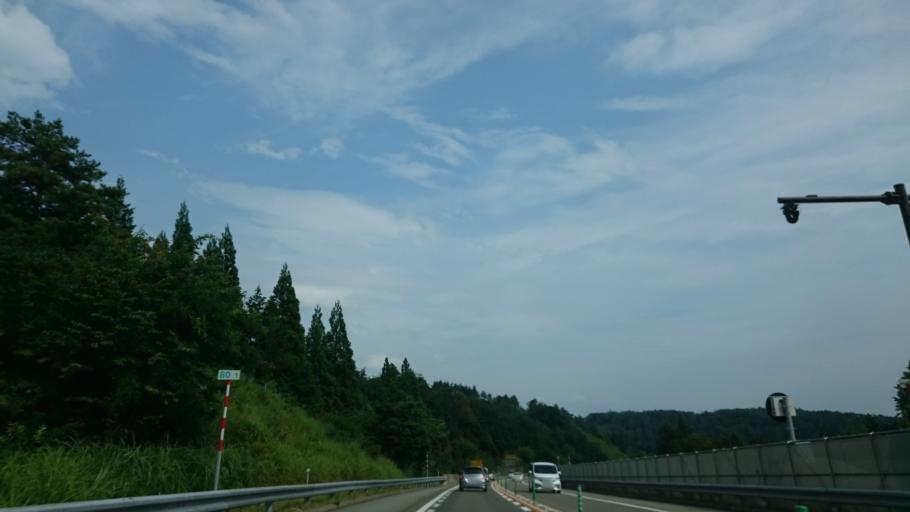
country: JP
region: Gifu
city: Gujo
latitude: 35.9023
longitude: 136.8750
